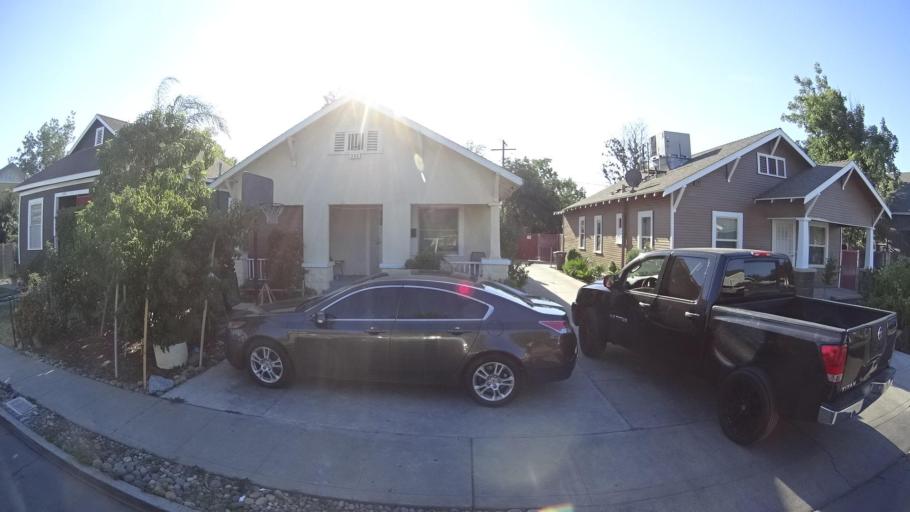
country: US
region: California
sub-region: Fresno County
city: Fresno
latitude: 36.7482
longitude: -119.7969
